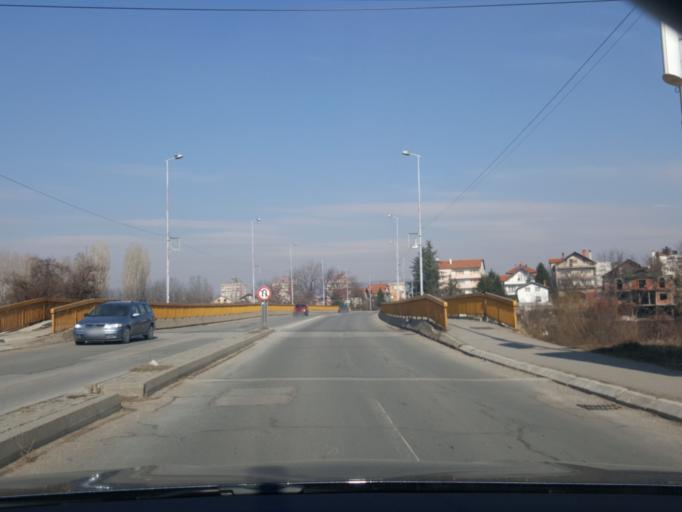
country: RS
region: Central Serbia
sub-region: Nisavski Okrug
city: Nis
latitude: 43.3244
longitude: 21.9259
